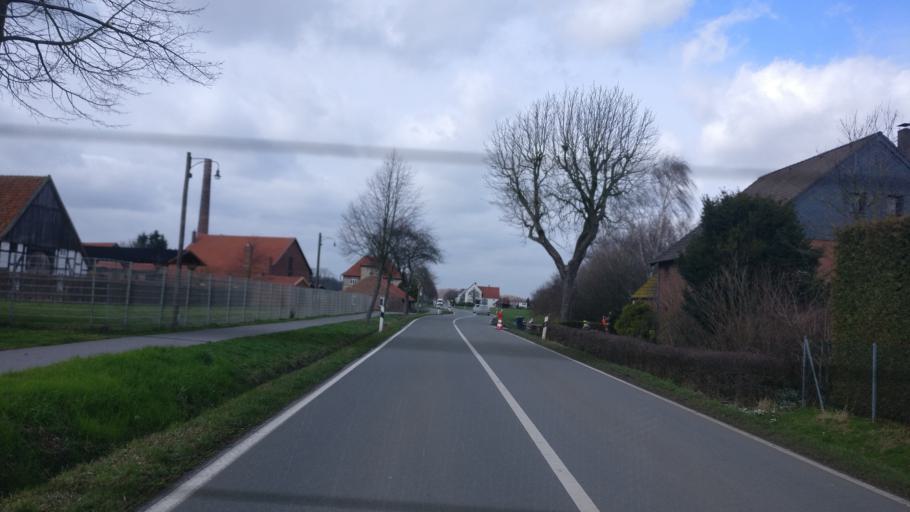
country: DE
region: North Rhine-Westphalia
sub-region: Regierungsbezirk Detmold
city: Lage
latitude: 52.0252
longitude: 8.7801
